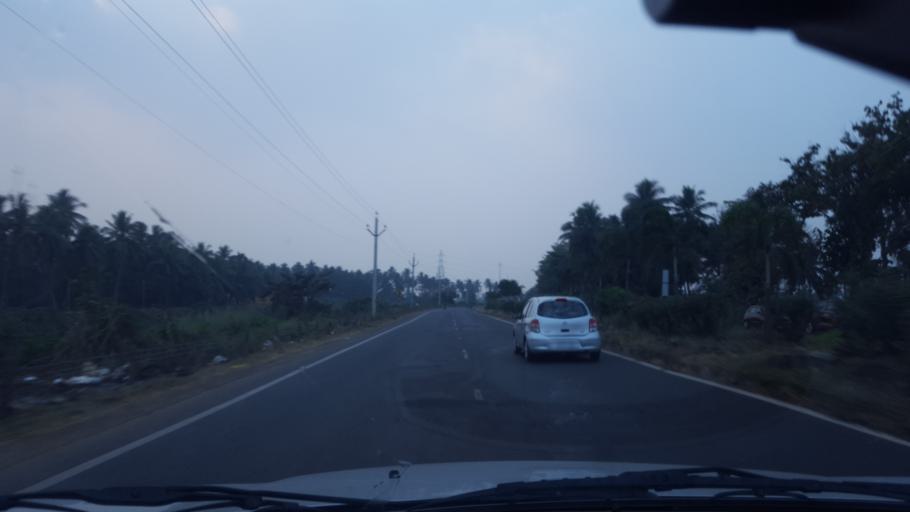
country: IN
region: Andhra Pradesh
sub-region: East Godavari
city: Rajahmundry
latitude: 16.8920
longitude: 81.8018
